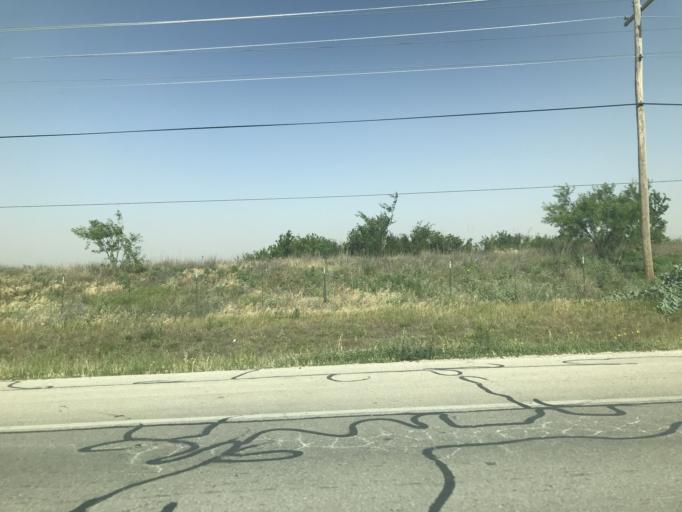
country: US
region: Texas
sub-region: Taylor County
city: Abilene
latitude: 32.3859
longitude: -99.7254
